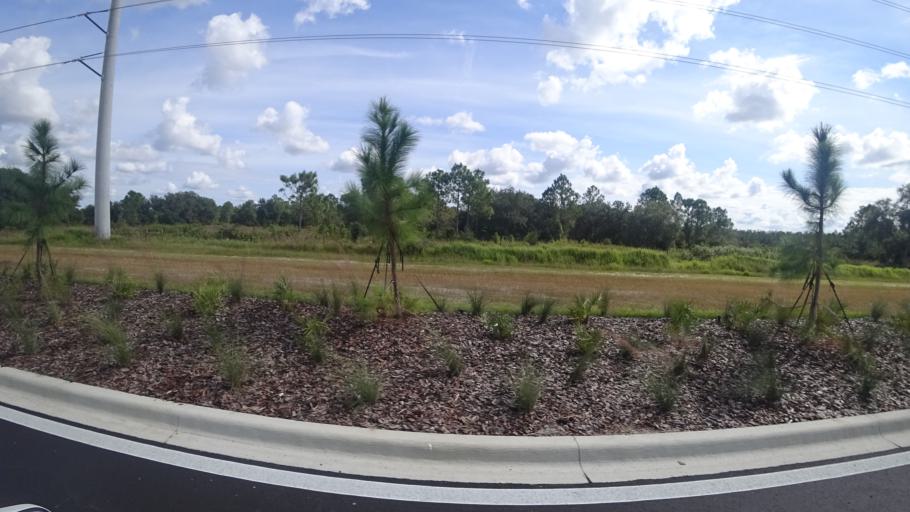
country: US
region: Florida
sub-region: Sarasota County
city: The Meadows
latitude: 27.4066
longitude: -82.3536
